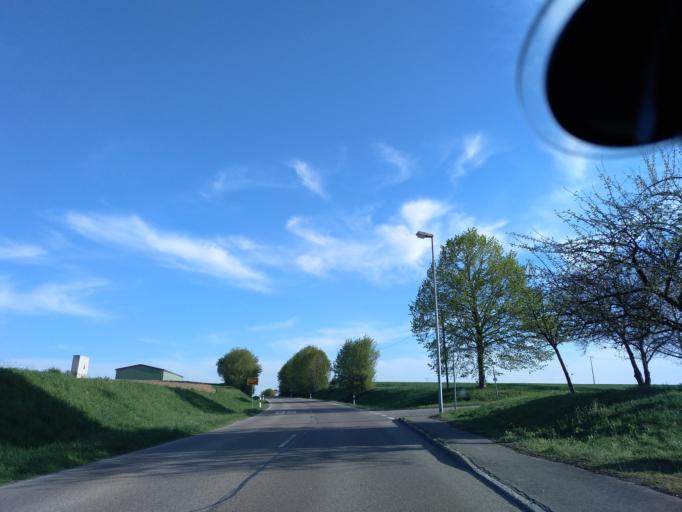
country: DE
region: Baden-Wuerttemberg
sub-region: Regierungsbezirk Stuttgart
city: Langenburg
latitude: 49.2239
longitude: 9.8483
